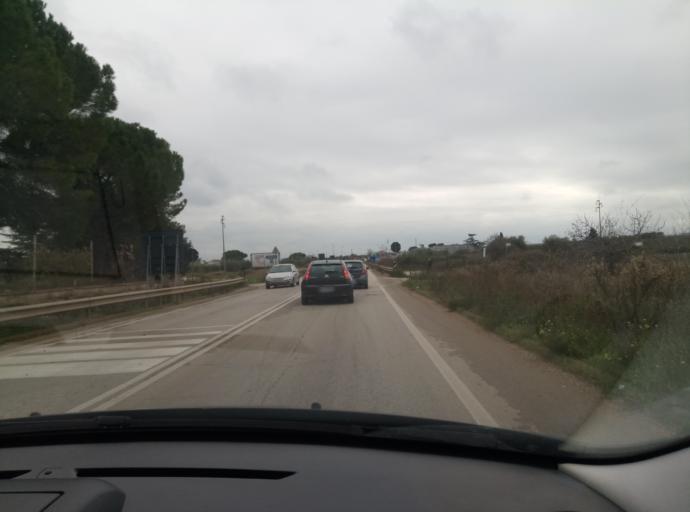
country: IT
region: Apulia
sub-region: Provincia di Bari
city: Acquaviva delle Fonti
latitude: 40.8988
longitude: 16.8322
